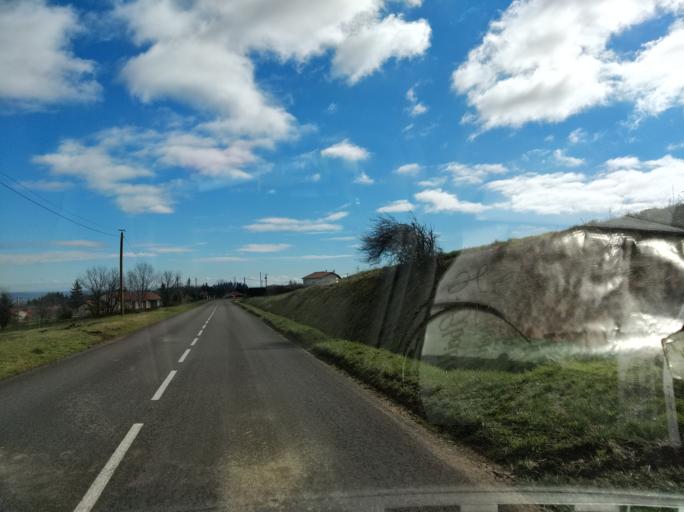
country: FR
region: Rhone-Alpes
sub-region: Departement de la Loire
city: Pelussin
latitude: 45.4116
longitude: 4.6769
